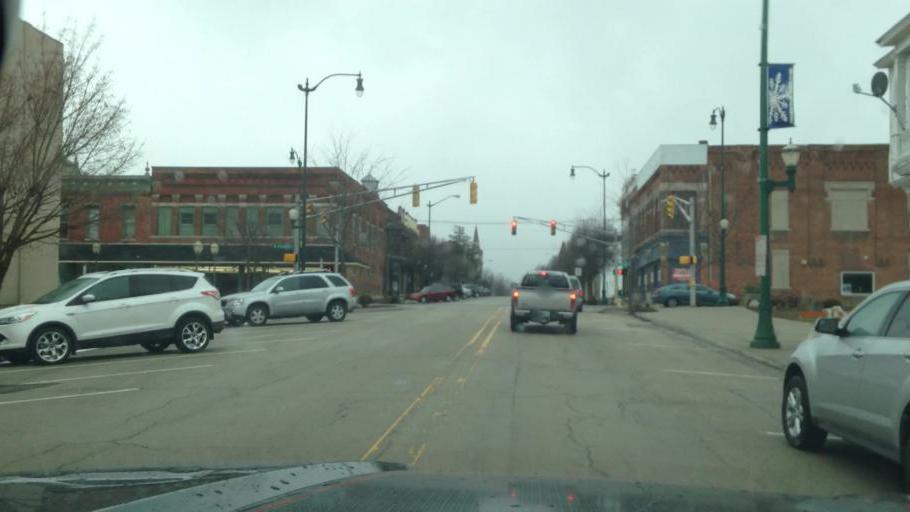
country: US
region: Indiana
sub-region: Randolph County
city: Union City
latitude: 40.2003
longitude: -84.8079
